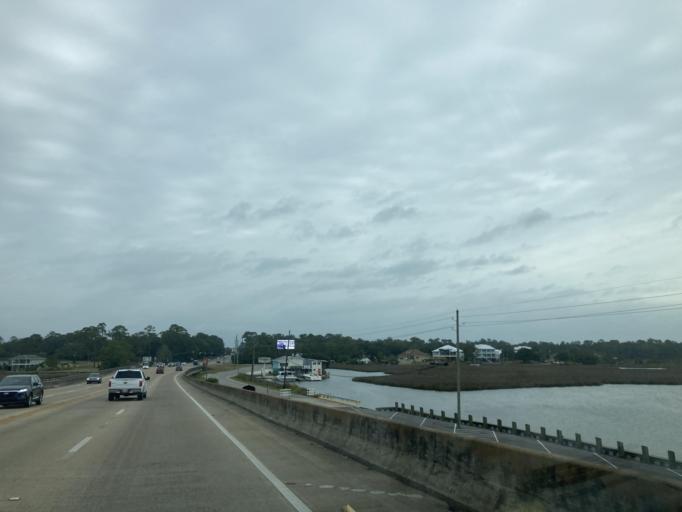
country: US
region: Mississippi
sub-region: Jackson County
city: Ocean Springs
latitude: 30.4207
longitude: -88.8283
